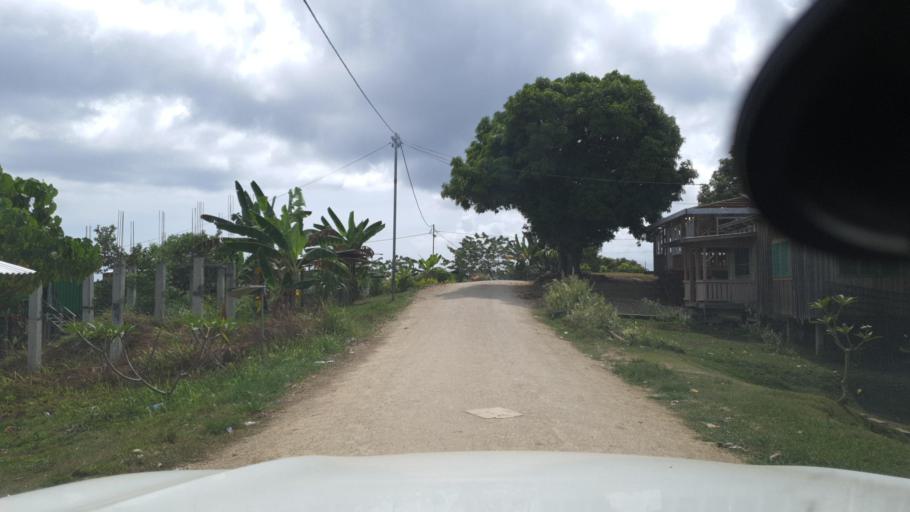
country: SB
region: Guadalcanal
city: Honiara
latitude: -9.4283
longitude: 159.9298
